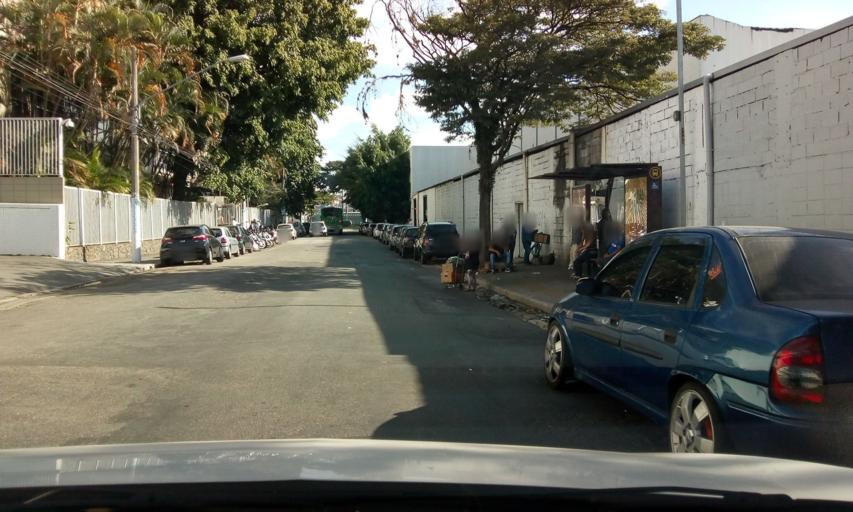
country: BR
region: Sao Paulo
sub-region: Osasco
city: Osasco
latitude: -23.5318
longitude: -46.7345
